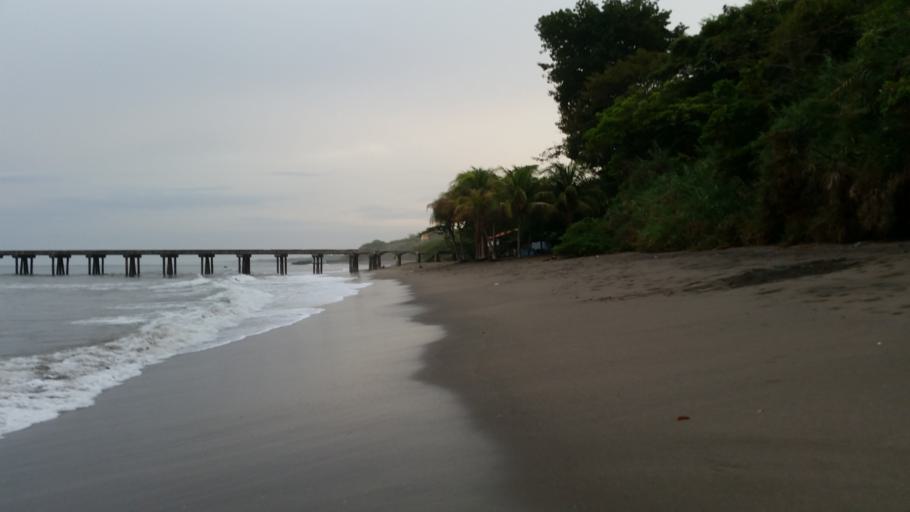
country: NI
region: Managua
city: Masachapa
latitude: 11.7946
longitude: -86.5178
